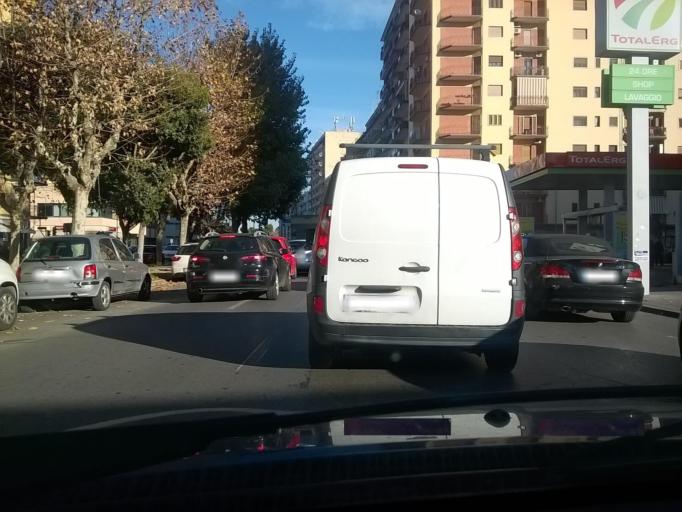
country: IT
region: Apulia
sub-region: Provincia di Taranto
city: Taranto
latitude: 40.4627
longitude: 17.2694
